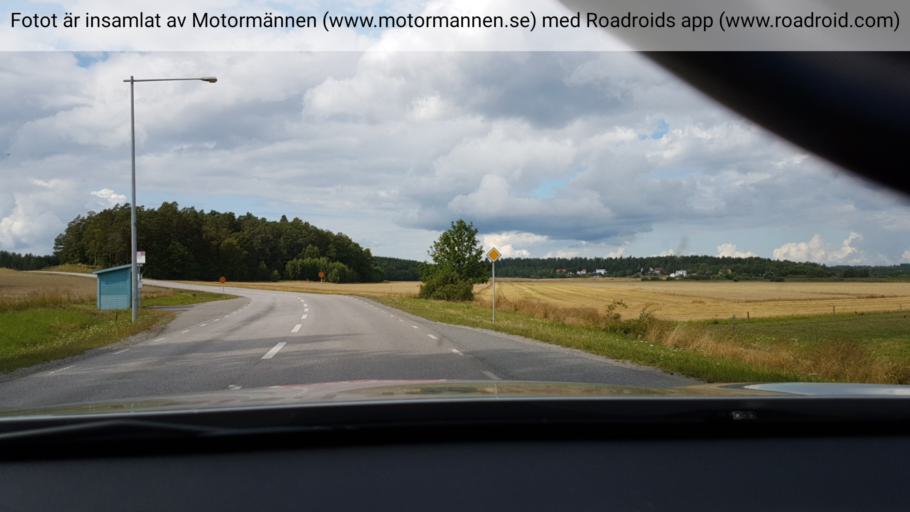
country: SE
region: Stockholm
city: Stenhamra
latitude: 59.3647
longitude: 17.7196
